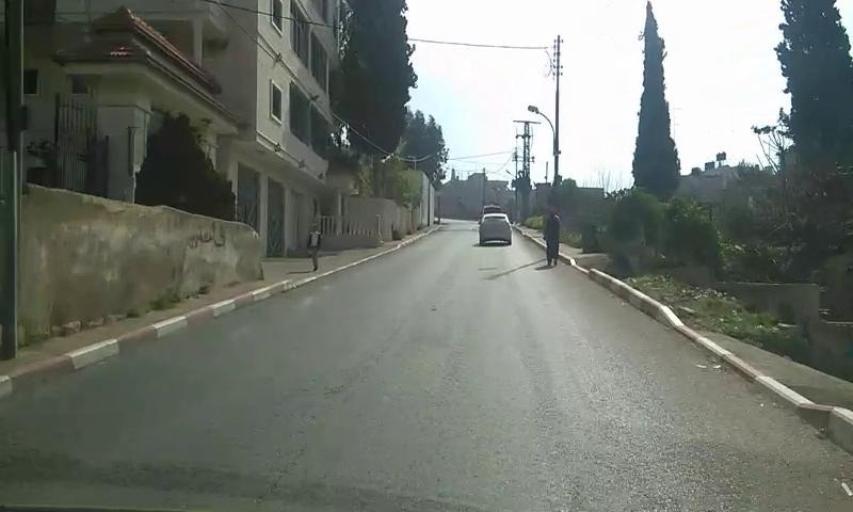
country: PS
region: West Bank
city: `Ayn Yabrud
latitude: 31.9542
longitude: 35.2489
